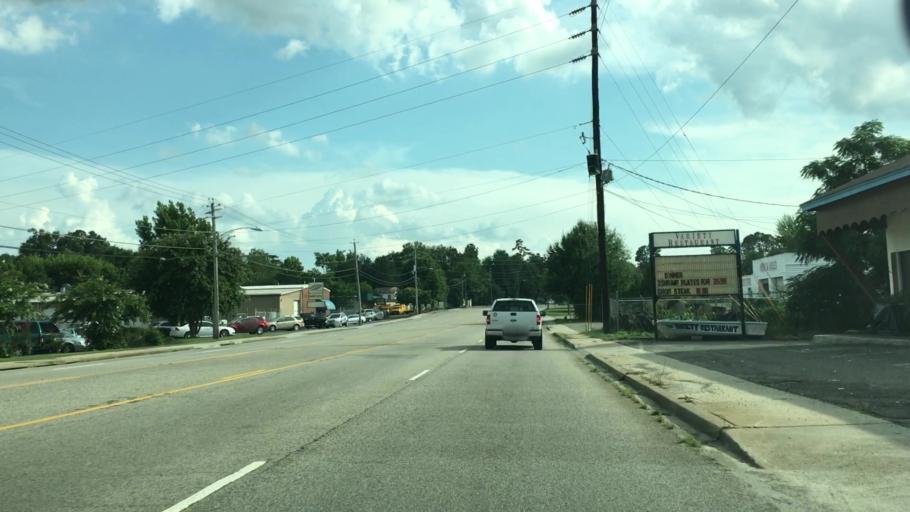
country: US
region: South Carolina
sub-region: Aiken County
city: Aiken
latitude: 33.5744
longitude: -81.7049
